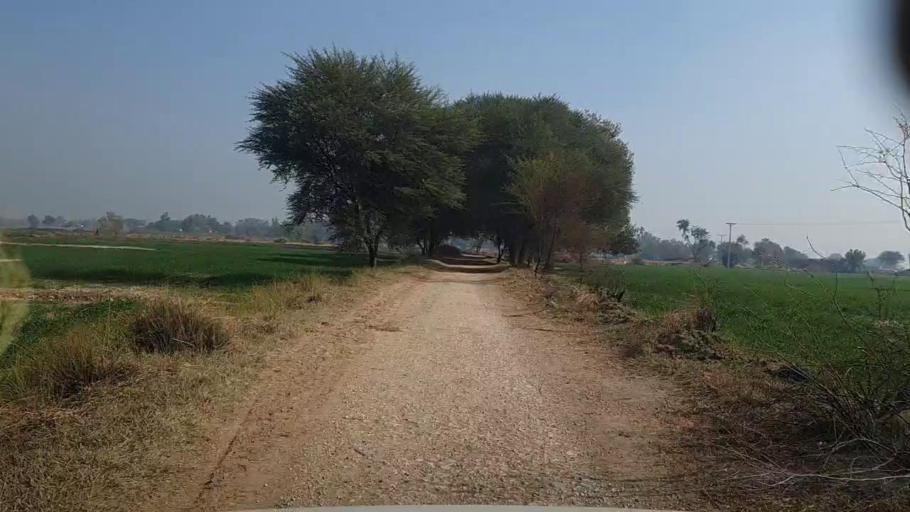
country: PK
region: Sindh
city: Khairpur
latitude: 27.9433
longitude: 69.6736
